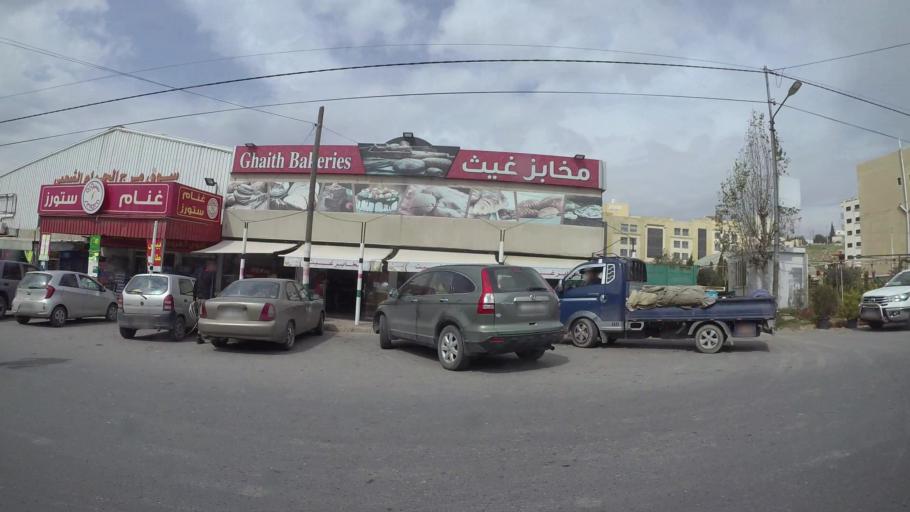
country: JO
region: Amman
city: Umm as Summaq
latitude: 31.9093
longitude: 35.8490
